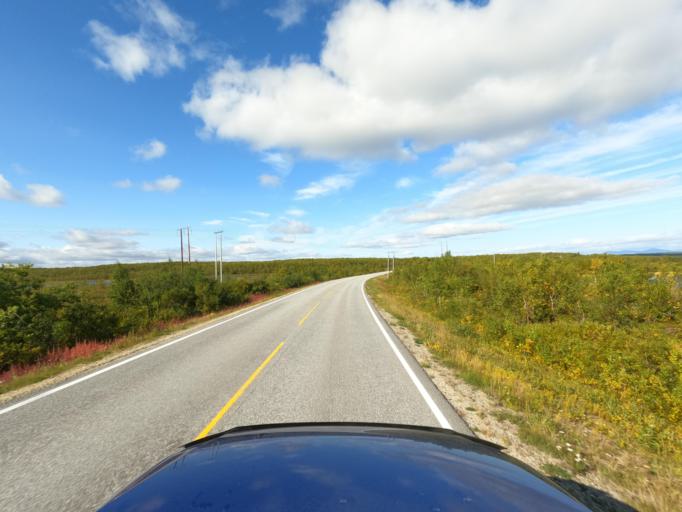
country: NO
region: Finnmark Fylke
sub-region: Karasjok
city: Karasjohka
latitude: 69.6109
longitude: 25.3089
